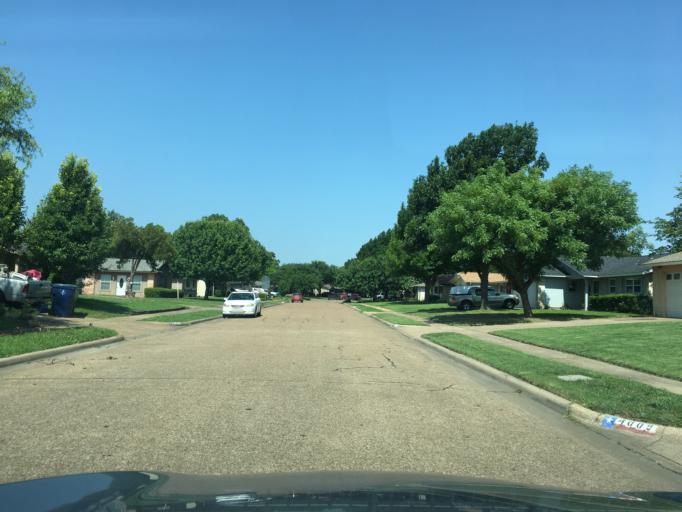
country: US
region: Texas
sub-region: Dallas County
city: Richardson
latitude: 32.9219
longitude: -96.6934
